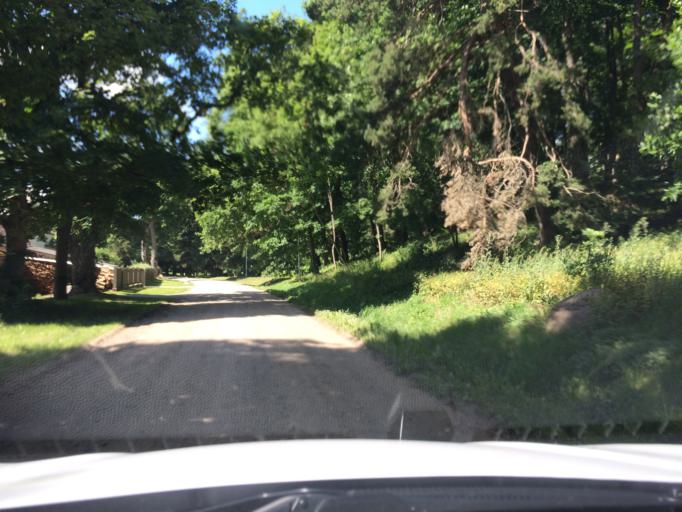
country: LV
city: Tervete
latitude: 56.4796
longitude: 23.3887
